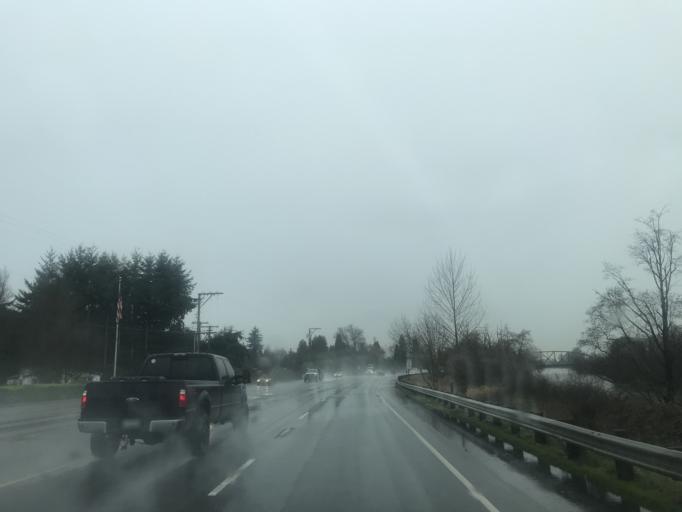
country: US
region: Washington
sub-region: Pierce County
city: Waller
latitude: 47.2106
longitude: -122.3351
